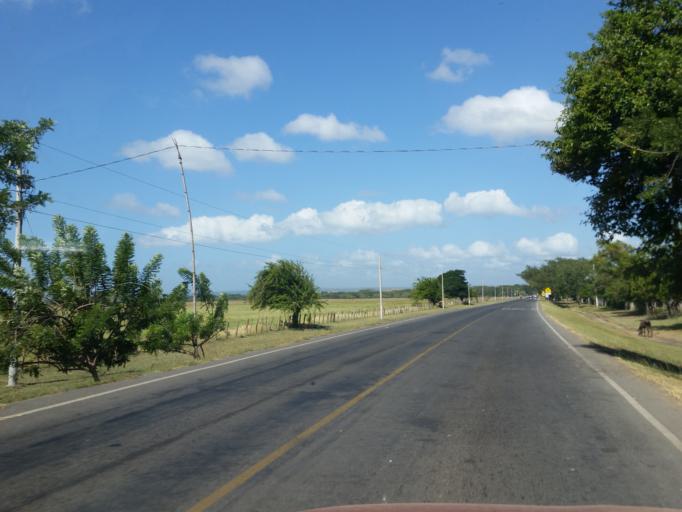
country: NI
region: Granada
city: Nandaime
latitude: 11.6993
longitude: -86.0010
